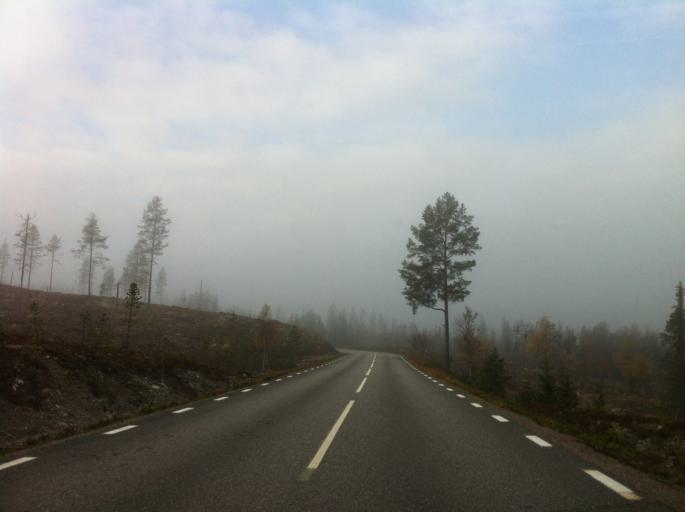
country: NO
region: Hedmark
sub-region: Engerdal
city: Engerdal
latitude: 61.9747
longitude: 12.5004
